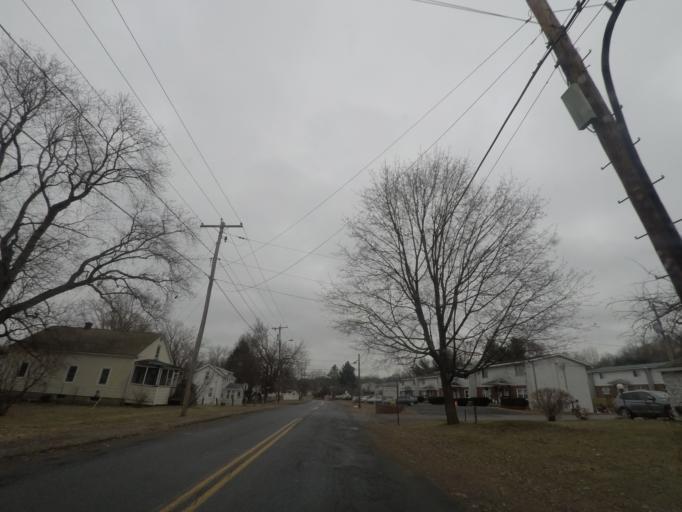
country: US
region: New York
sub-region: Saratoga County
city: Waterford
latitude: 42.7950
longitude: -73.6626
